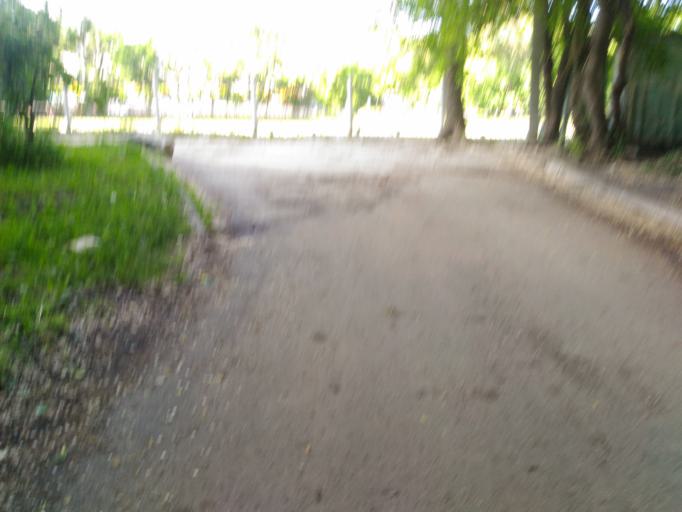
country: RU
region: Ulyanovsk
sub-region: Ulyanovskiy Rayon
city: Ulyanovsk
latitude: 54.3218
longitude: 48.3856
